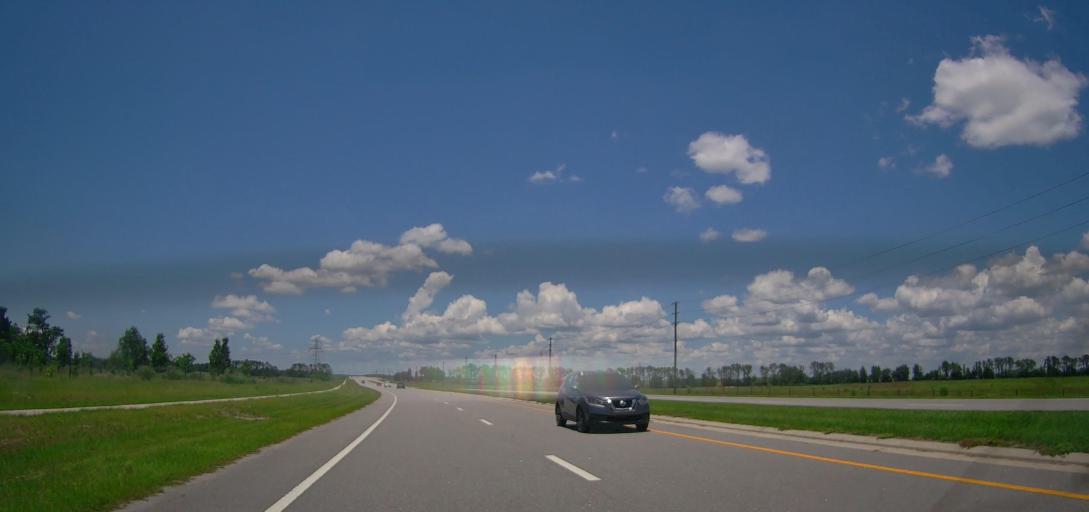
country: US
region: Florida
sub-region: Marion County
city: Silver Springs Shores
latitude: 29.0652
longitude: -82.0193
